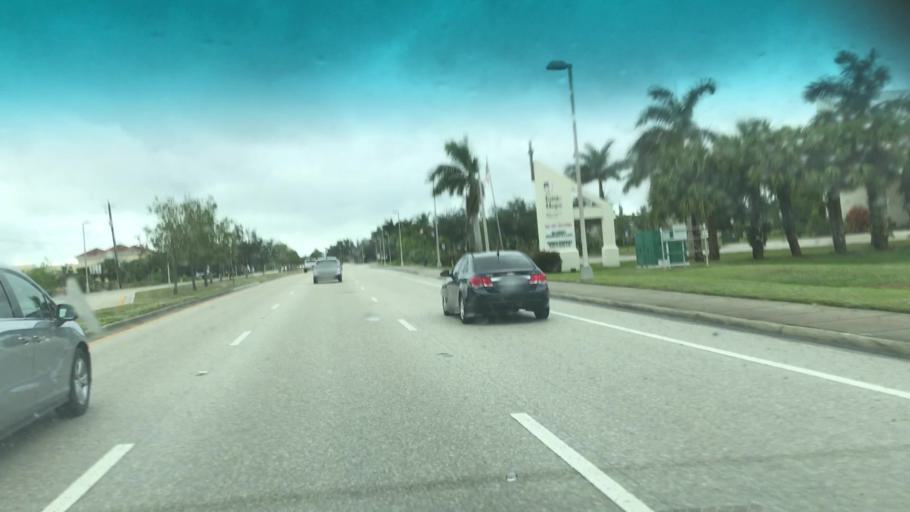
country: US
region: Florida
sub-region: Lee County
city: Harlem Heights
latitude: 26.5204
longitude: -81.9126
